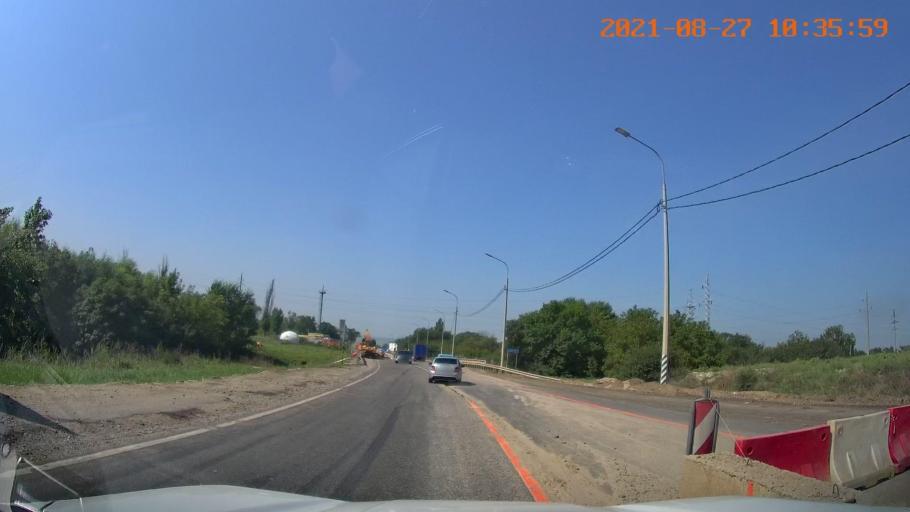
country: RU
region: Karachayevo-Cherkesiya
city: Cherkessk
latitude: 44.2531
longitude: 42.0915
